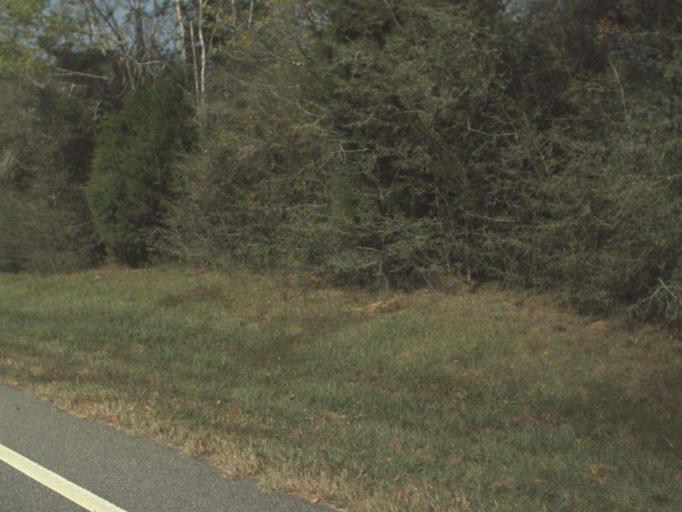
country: US
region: Alabama
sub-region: Geneva County
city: Geneva
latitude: 30.9465
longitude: -85.7563
